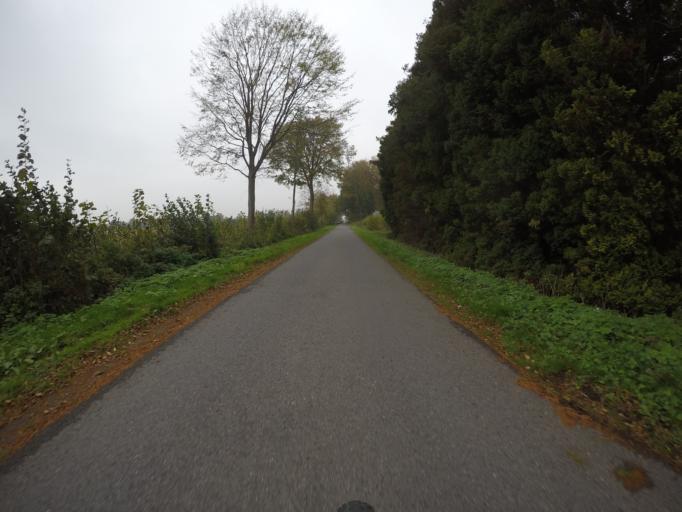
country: DE
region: North Rhine-Westphalia
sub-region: Regierungsbezirk Dusseldorf
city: Bocholt
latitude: 51.8324
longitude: 6.5567
